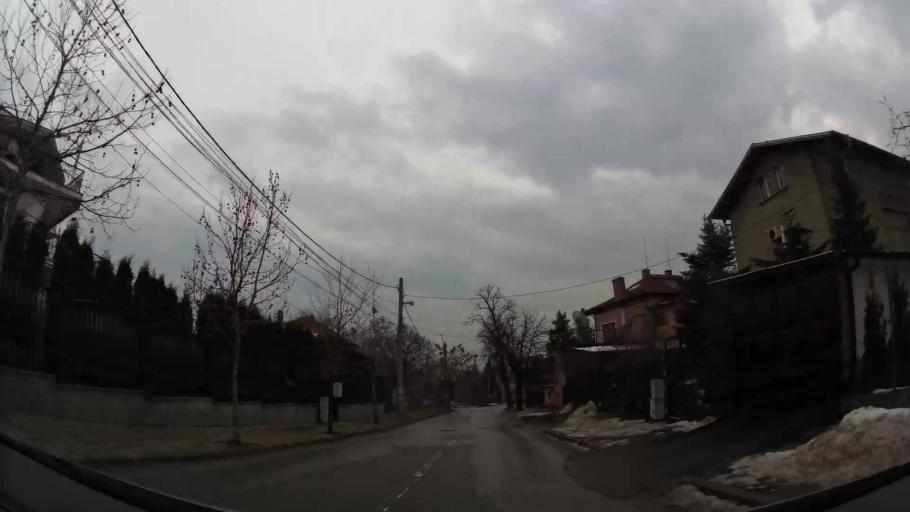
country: BG
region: Sofiya
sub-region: Obshtina Bozhurishte
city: Bozhurishte
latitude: 42.6752
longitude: 23.2357
